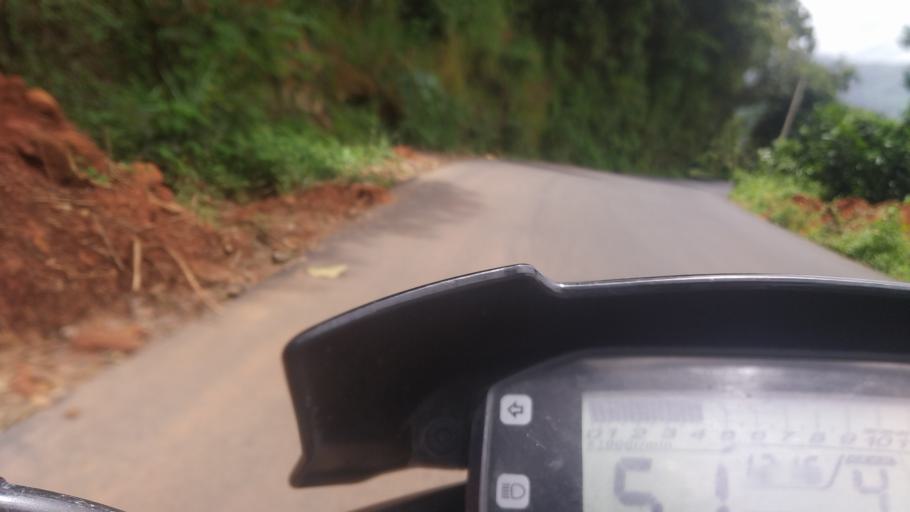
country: IN
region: Kerala
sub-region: Idukki
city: Munnar
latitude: 10.0160
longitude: 77.0123
